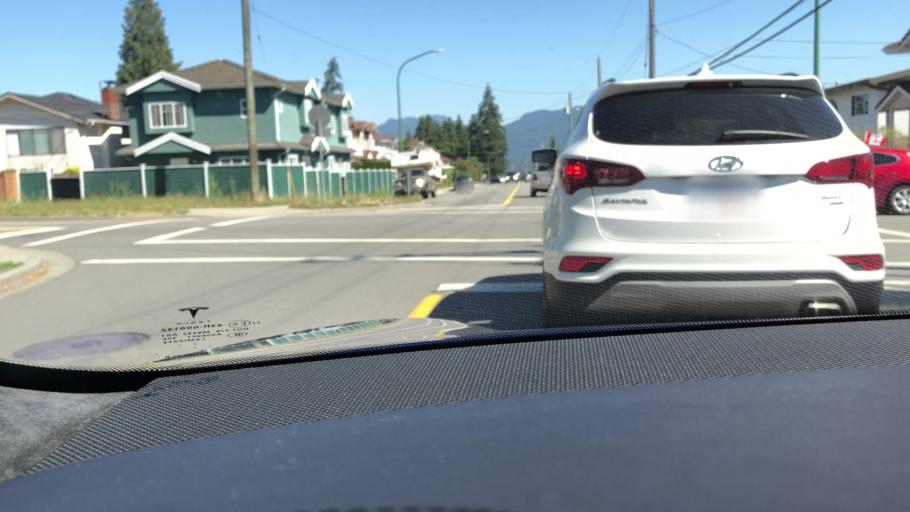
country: CA
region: British Columbia
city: Burnaby
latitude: 49.2218
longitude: -122.9720
